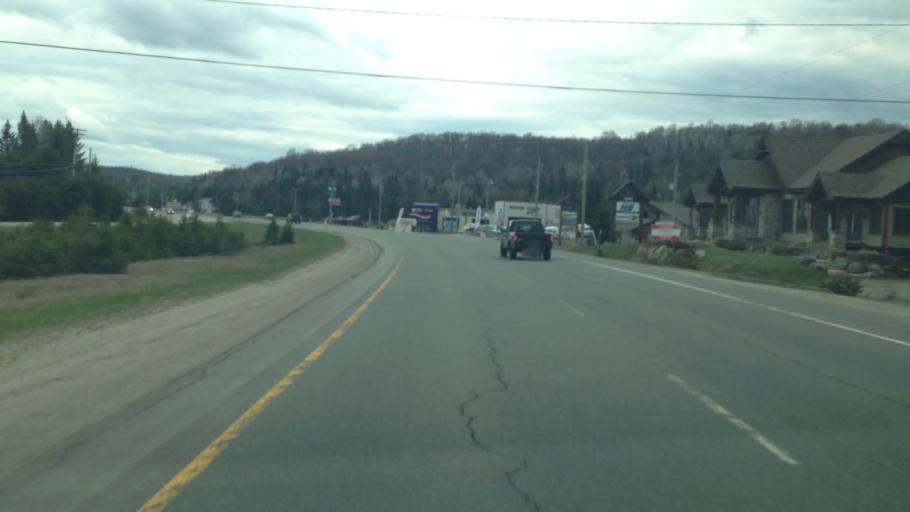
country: CA
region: Quebec
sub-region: Laurentides
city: Sainte-Agathe-des-Monts
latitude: 46.0757
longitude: -74.3154
